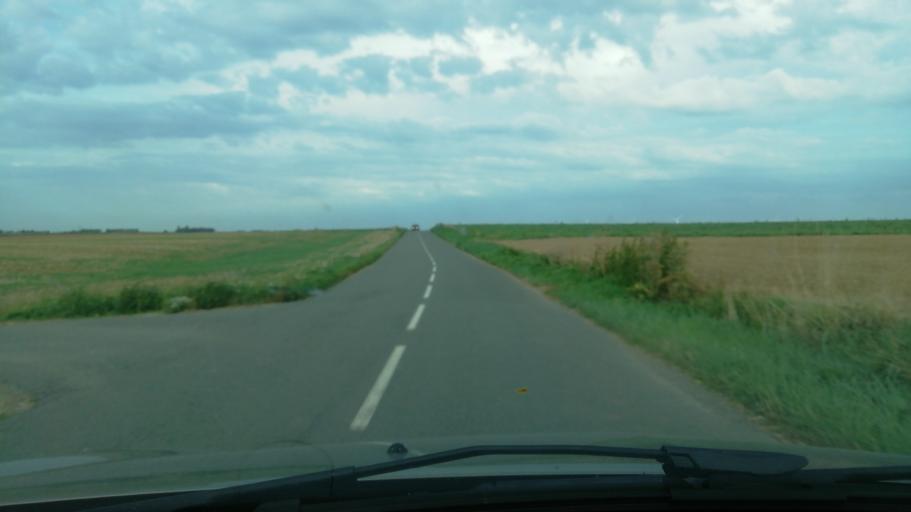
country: FR
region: Nord-Pas-de-Calais
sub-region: Departement du Nord
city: Avesnes-les-Aubert
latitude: 50.1693
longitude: 3.3761
